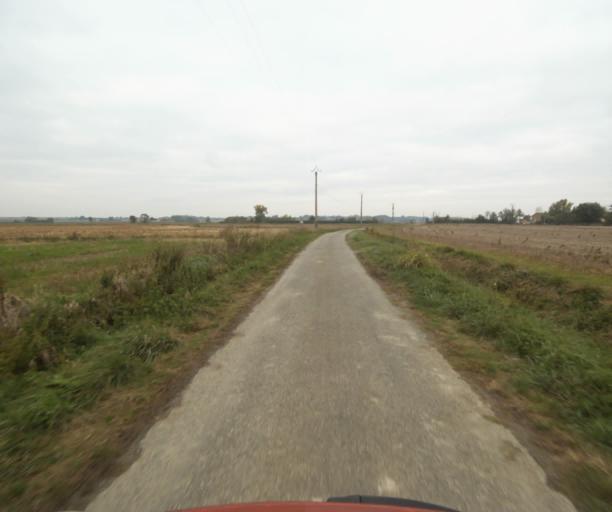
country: FR
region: Midi-Pyrenees
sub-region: Departement du Tarn-et-Garonne
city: Verdun-sur-Garonne
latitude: 43.8156
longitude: 1.2265
